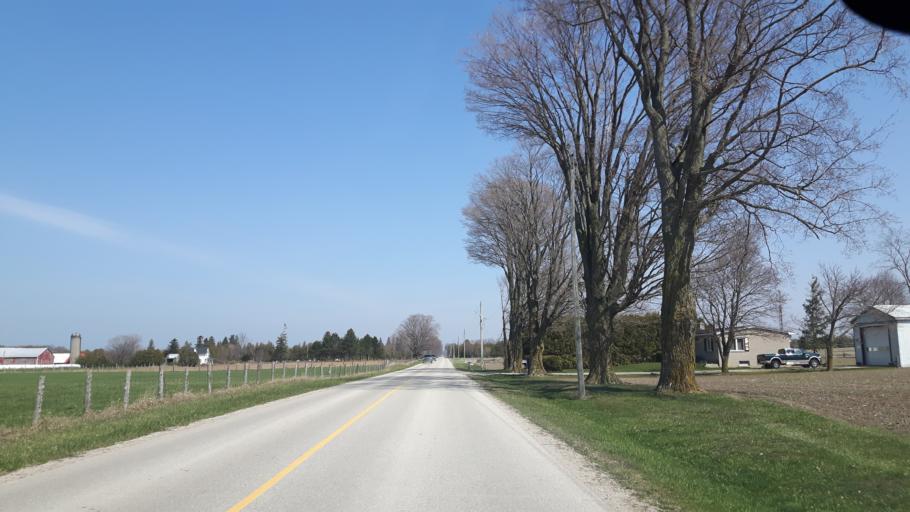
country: CA
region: Ontario
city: Goderich
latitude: 43.6618
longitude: -81.6846
